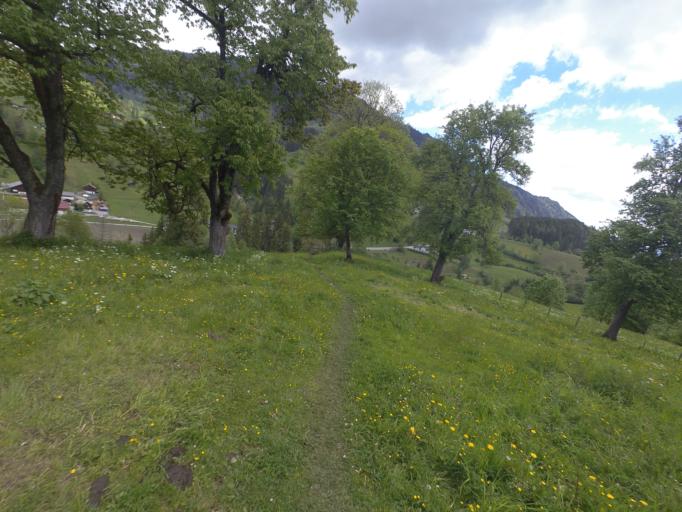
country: AT
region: Salzburg
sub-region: Politischer Bezirk Sankt Johann im Pongau
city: Goldegg
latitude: 47.3303
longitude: 13.1192
